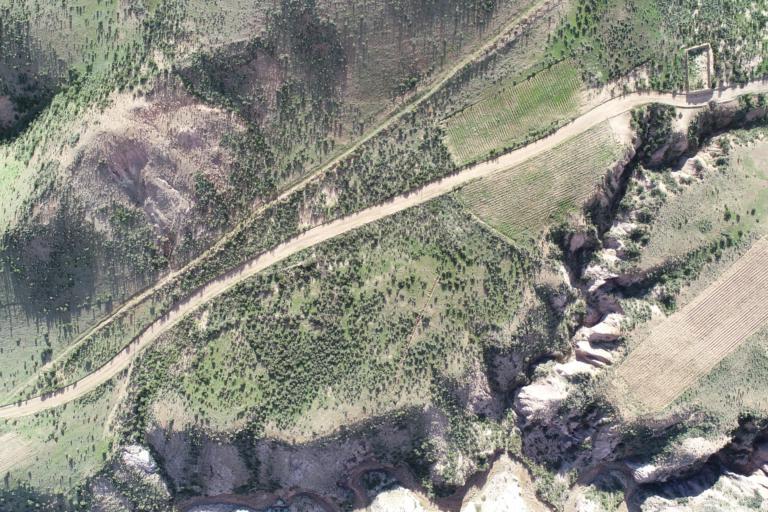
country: BO
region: La Paz
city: Curahuara de Carangas
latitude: -17.2987
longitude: -68.4903
